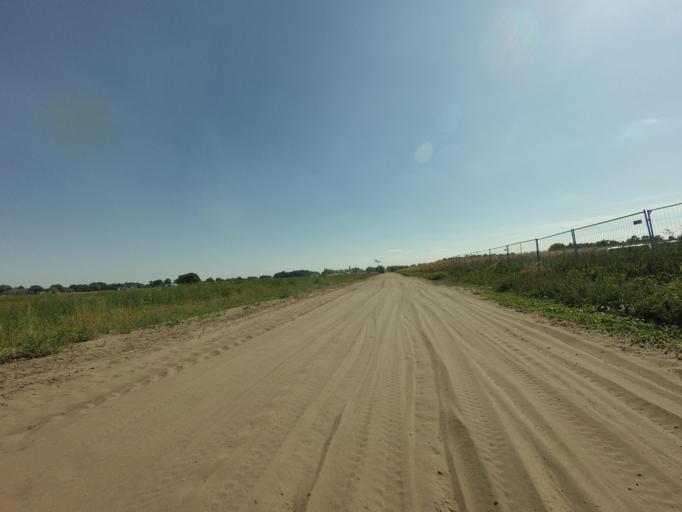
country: NL
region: North Brabant
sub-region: Gemeente Someren
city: Someren
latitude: 51.3845
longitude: 5.6684
